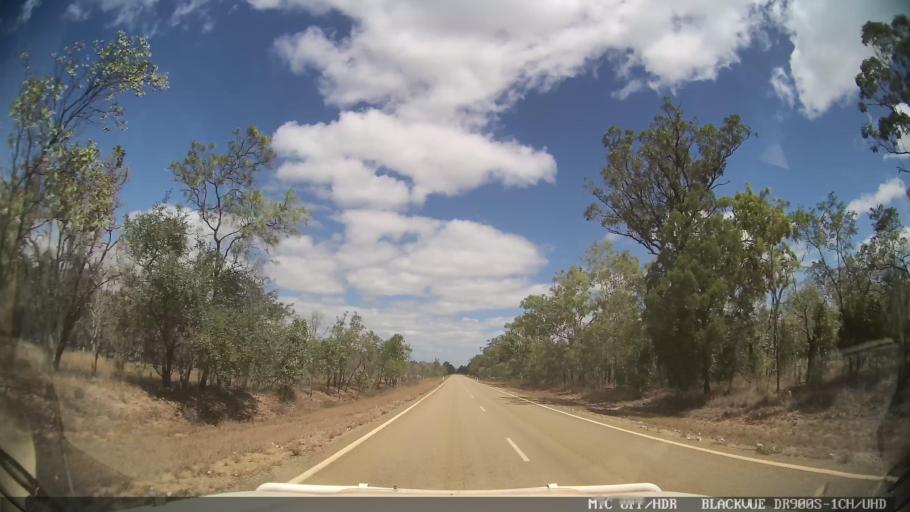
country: AU
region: Queensland
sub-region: Tablelands
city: Ravenshoe
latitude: -17.8126
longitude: 144.9573
